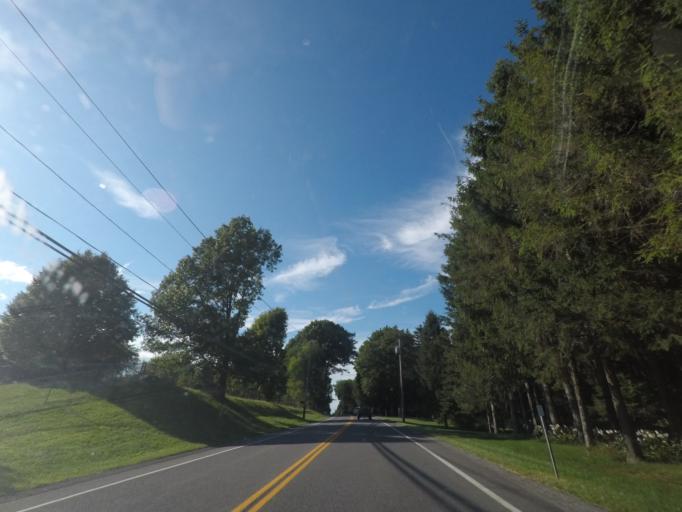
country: US
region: New York
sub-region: Albany County
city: West Albany
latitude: 42.7067
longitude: -73.7564
